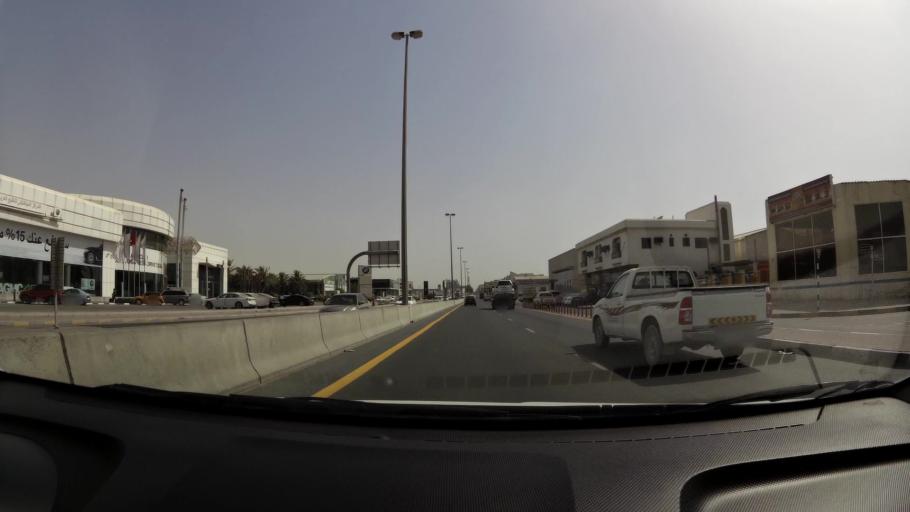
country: AE
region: Ash Shariqah
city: Sharjah
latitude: 25.3196
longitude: 55.4287
